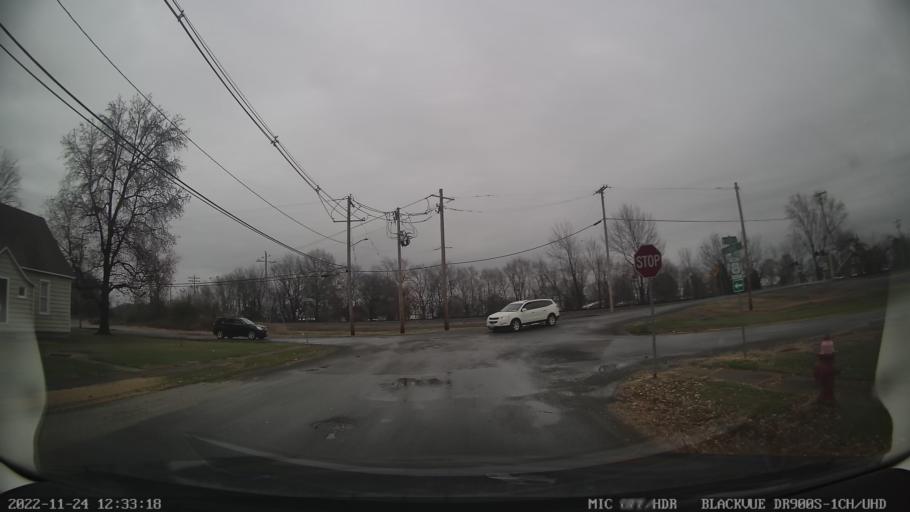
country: US
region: Illinois
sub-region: Macoupin County
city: Staunton
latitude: 39.0188
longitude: -89.7739
